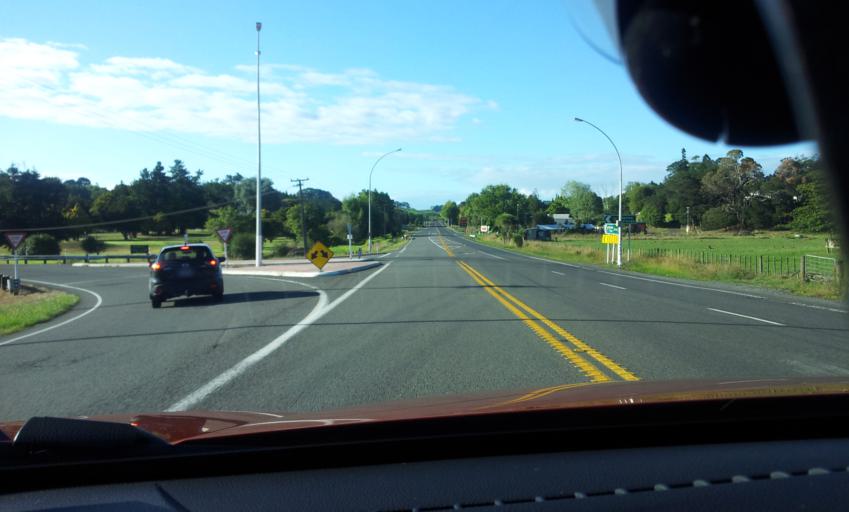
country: NZ
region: Waikato
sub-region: Hauraki District
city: Ngatea
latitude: -37.2907
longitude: 175.3712
